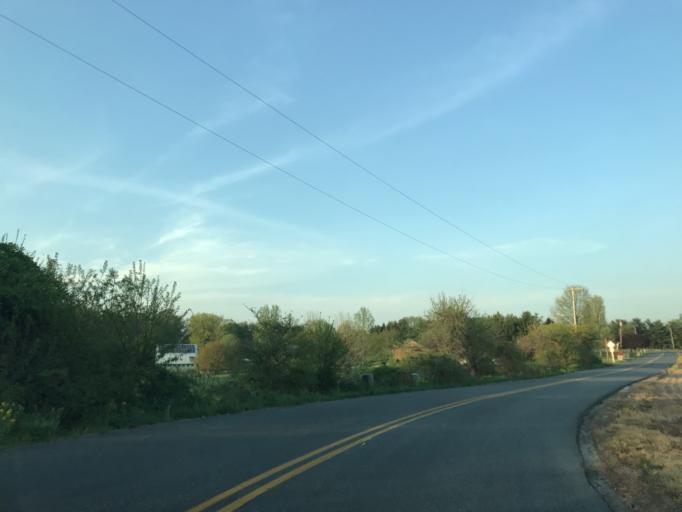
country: US
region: Maryland
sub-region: Harford County
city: Jarrettsville
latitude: 39.6164
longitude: -76.4911
